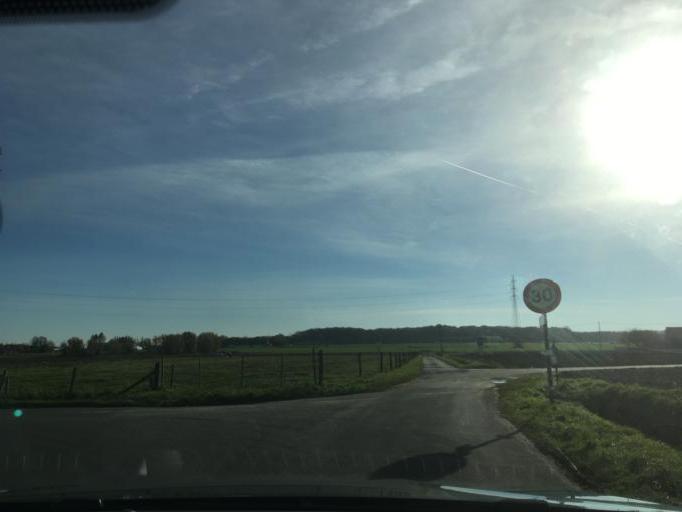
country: BE
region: Flanders
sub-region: Provincie West-Vlaanderen
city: Pittem
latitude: 50.9752
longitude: 3.2341
